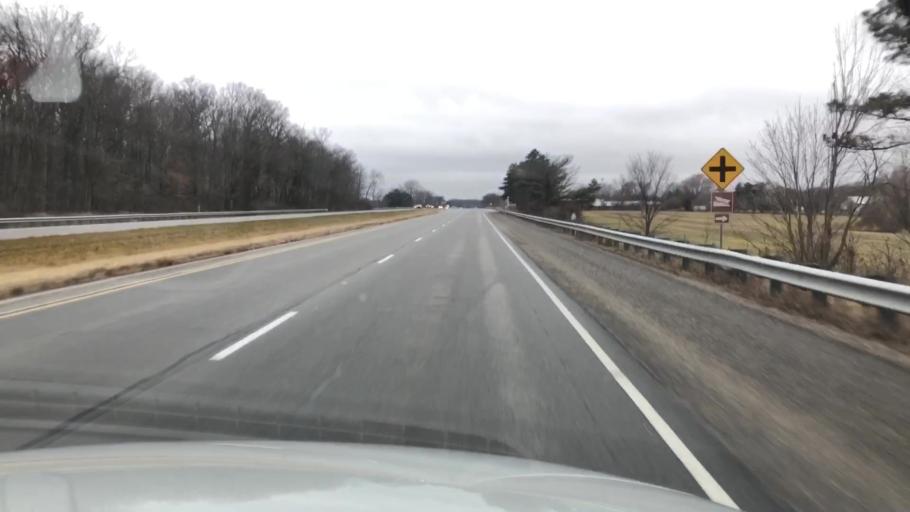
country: US
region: Indiana
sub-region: Whitley County
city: Churubusco
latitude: 41.1260
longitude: -85.3095
